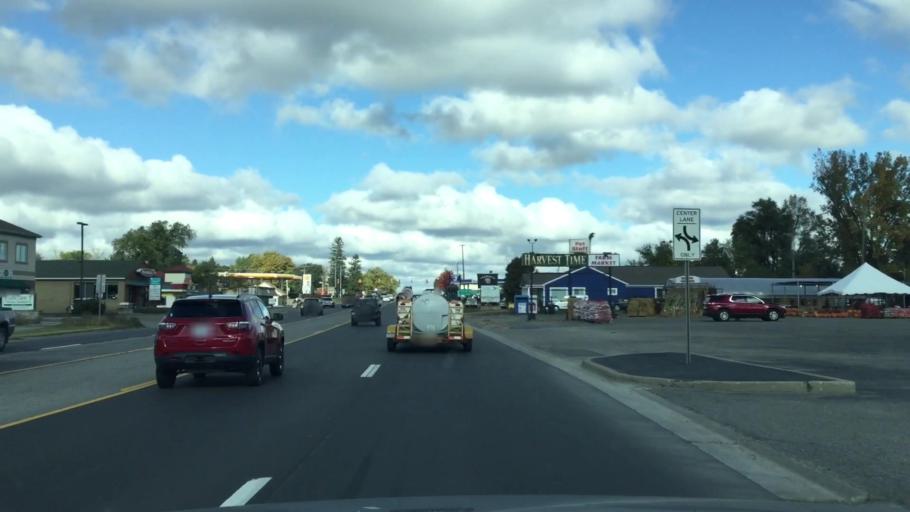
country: US
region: Michigan
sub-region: Oakland County
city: Oxford
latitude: 42.8084
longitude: -83.2499
